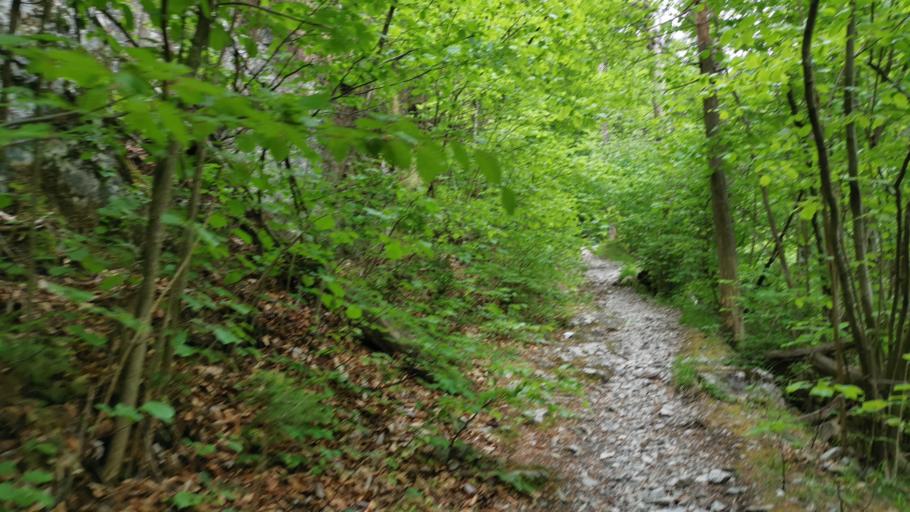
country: AT
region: Styria
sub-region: Politischer Bezirk Weiz
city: Mortantsch
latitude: 47.2330
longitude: 15.5580
